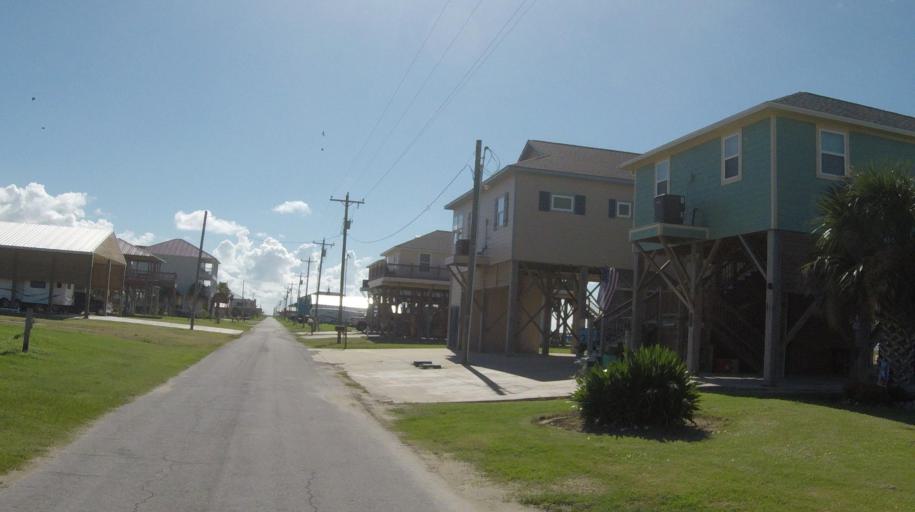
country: US
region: Louisiana
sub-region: Cameron Parish
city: Cameron
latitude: 29.7706
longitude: -93.4580
